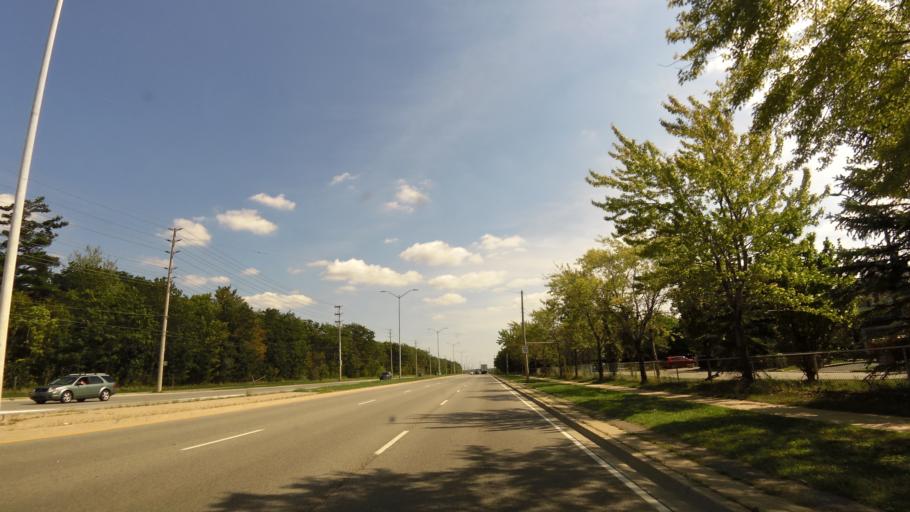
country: CA
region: Ontario
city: Mississauga
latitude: 43.5672
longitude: -79.7183
